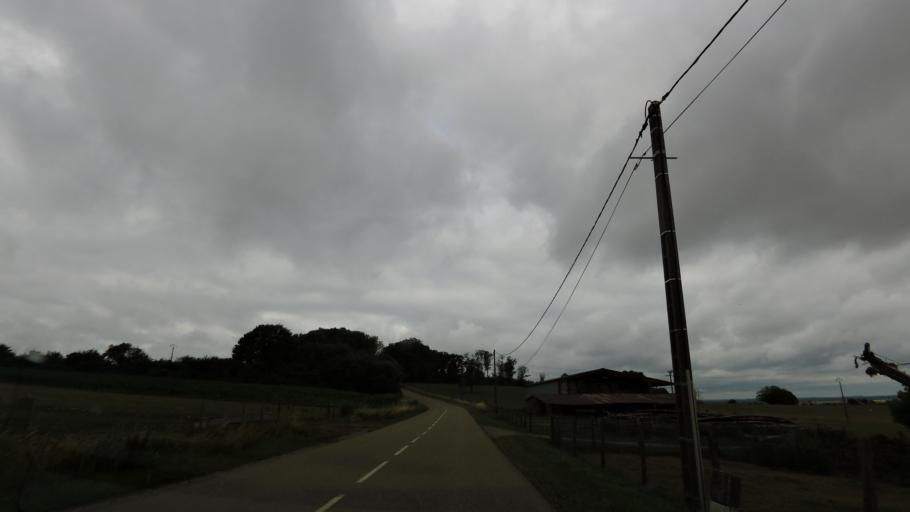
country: FR
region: Lorraine
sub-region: Departement de la Moselle
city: Lorquin
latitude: 48.6422
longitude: 6.9416
